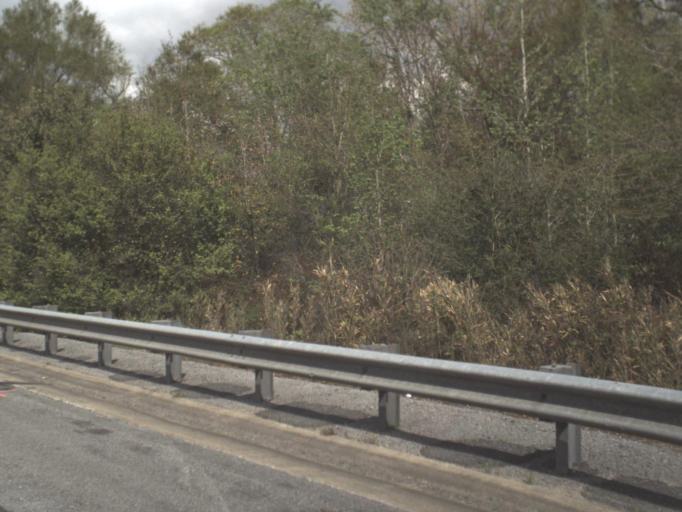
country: US
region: Florida
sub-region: Okaloosa County
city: Crestview
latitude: 30.7160
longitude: -86.6454
